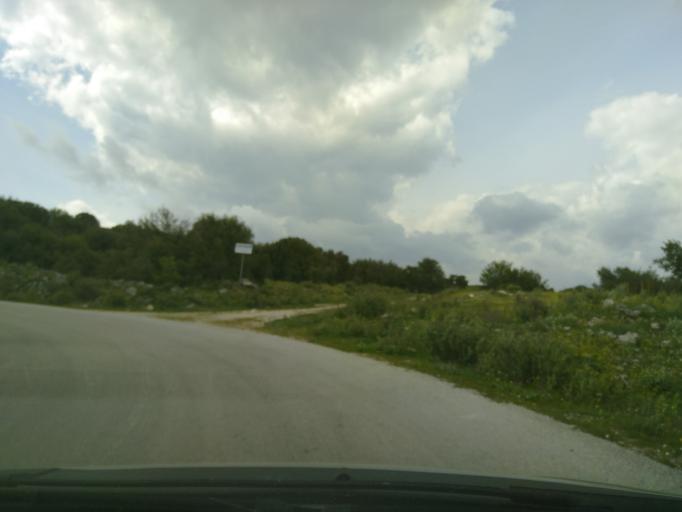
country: GR
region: Epirus
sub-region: Nomos Ioanninon
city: Asprangeloi
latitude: 39.7759
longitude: 20.6979
